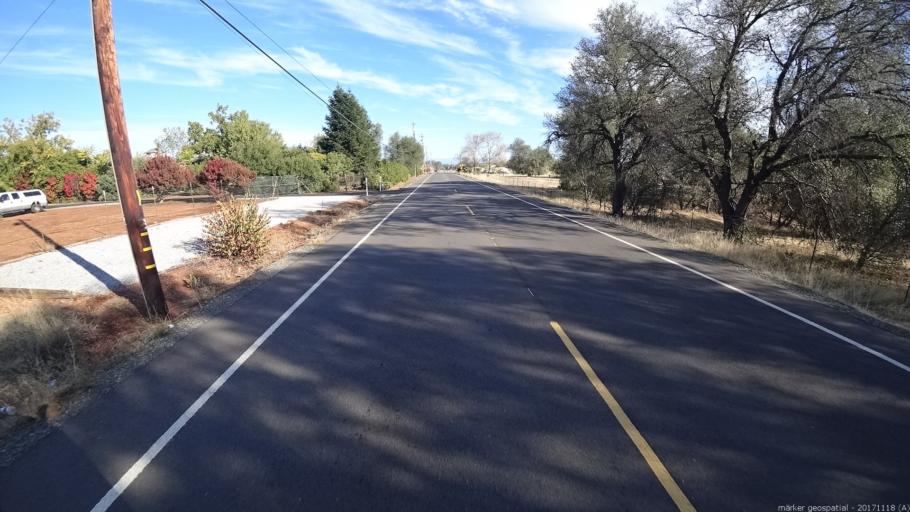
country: US
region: California
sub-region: Shasta County
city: Anderson
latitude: 40.4779
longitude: -122.4013
